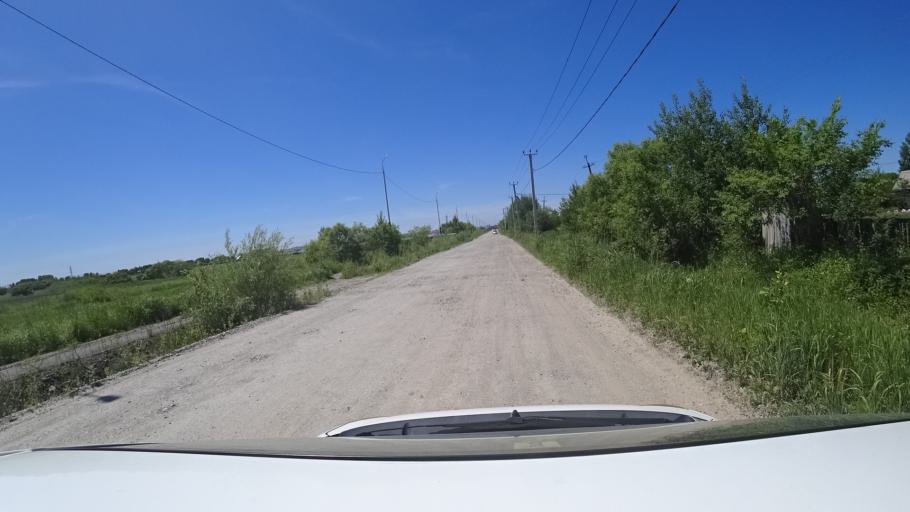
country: RU
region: Khabarovsk Krai
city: Topolevo
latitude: 48.5010
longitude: 135.1911
